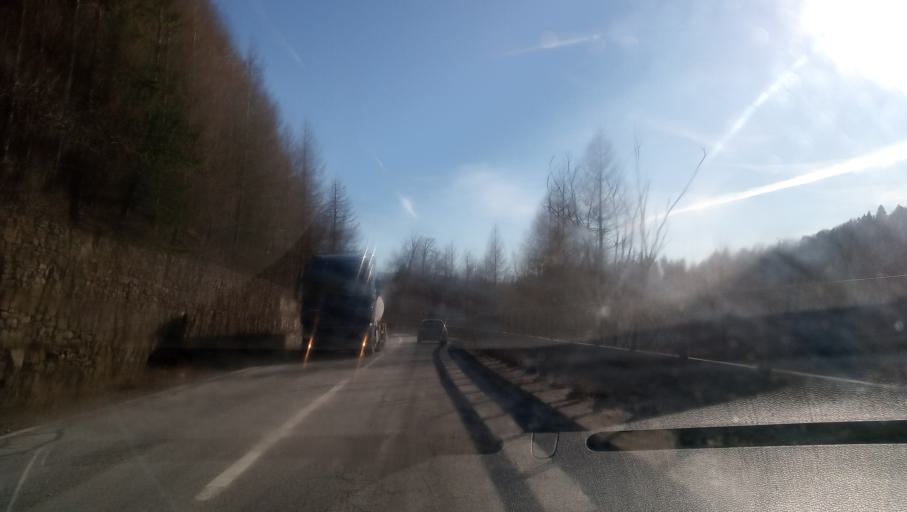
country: RO
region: Brasov
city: Crivina
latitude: 45.4710
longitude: 25.9215
